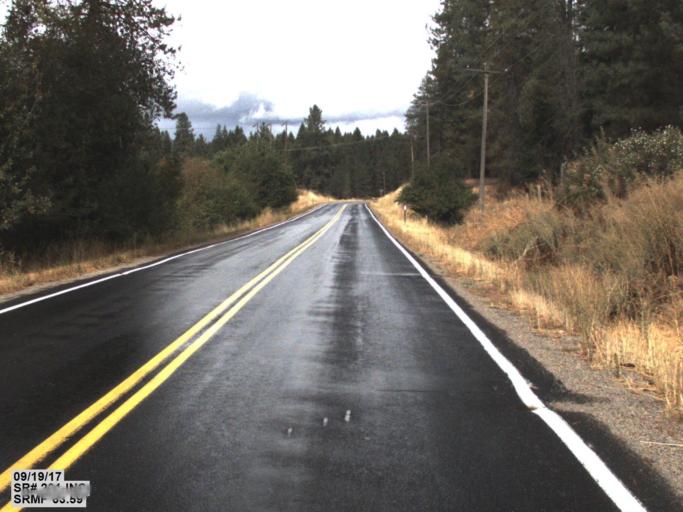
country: US
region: Washington
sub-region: Stevens County
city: Chewelah
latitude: 48.0657
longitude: -117.7631
